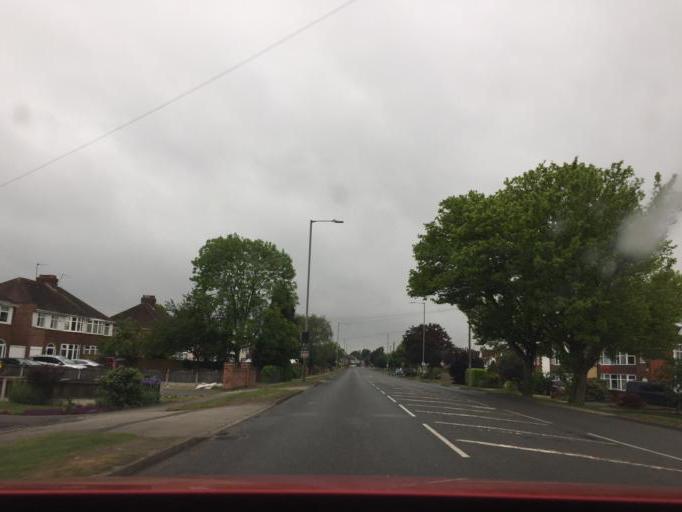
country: GB
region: England
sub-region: Warwickshire
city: Attleborough
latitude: 52.5335
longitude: -1.4240
